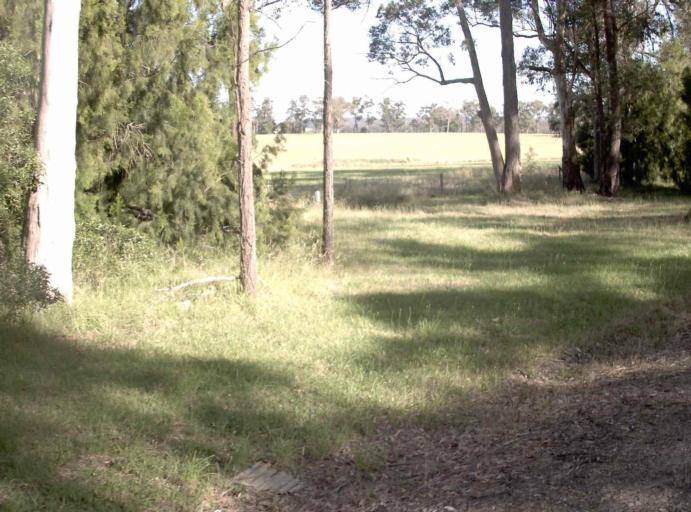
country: AU
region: Victoria
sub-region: East Gippsland
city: Lakes Entrance
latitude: -37.6863
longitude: 148.4694
